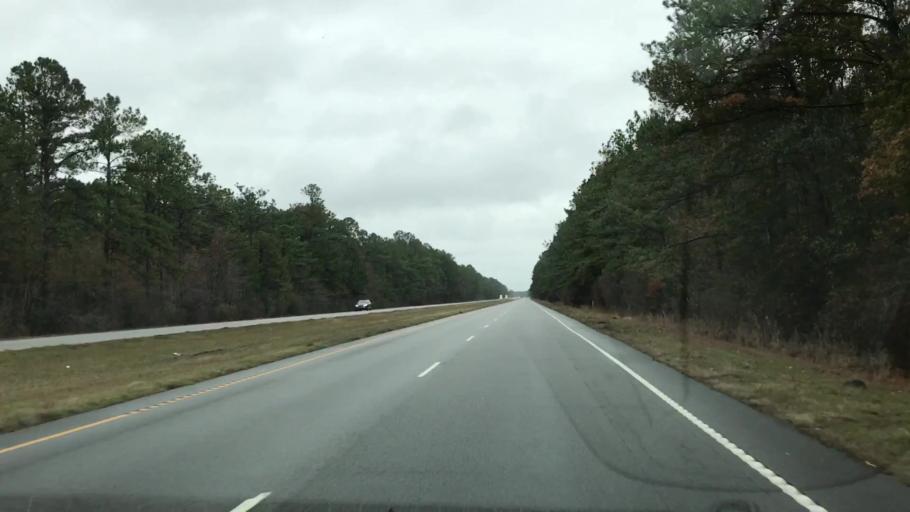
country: US
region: South Carolina
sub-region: Charleston County
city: Awendaw
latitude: 33.1574
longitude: -79.4283
